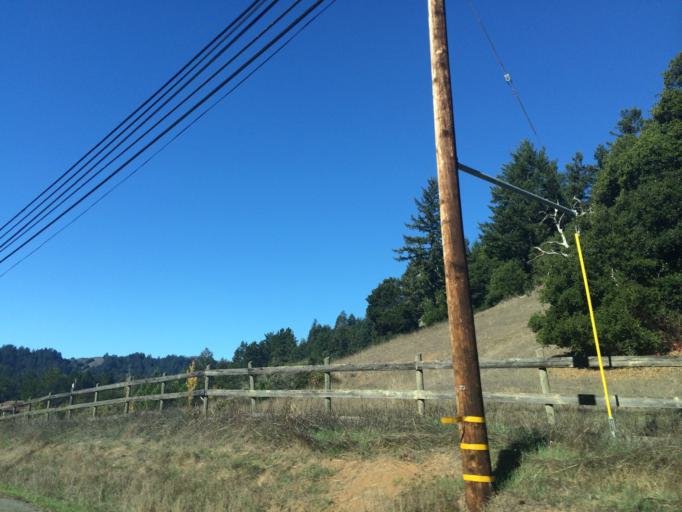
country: US
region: California
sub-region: Marin County
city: Lagunitas-Forest Knolls
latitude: 38.0162
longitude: -122.6826
